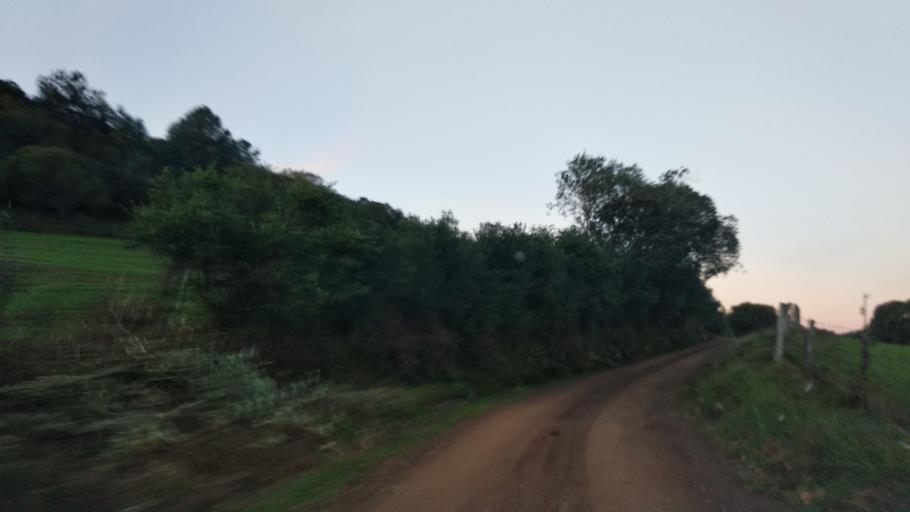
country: BR
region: Santa Catarina
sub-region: Celso Ramos
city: Celso Ramos
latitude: -27.5582
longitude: -51.2268
